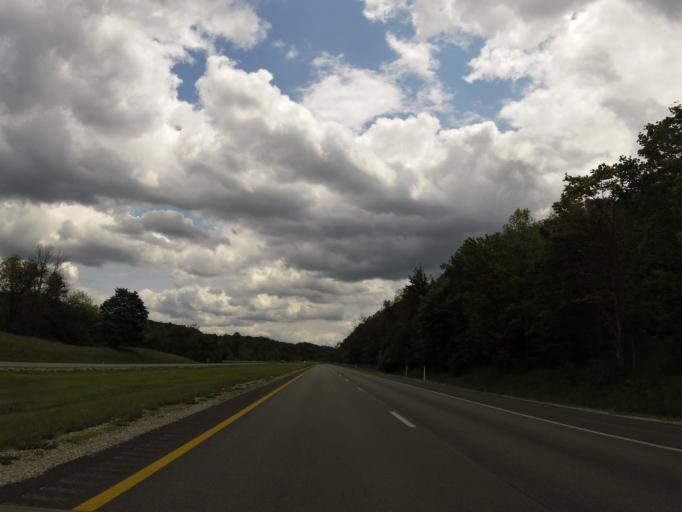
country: US
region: West Virginia
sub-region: Jackson County
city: Ripley
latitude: 38.7288
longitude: -81.6577
